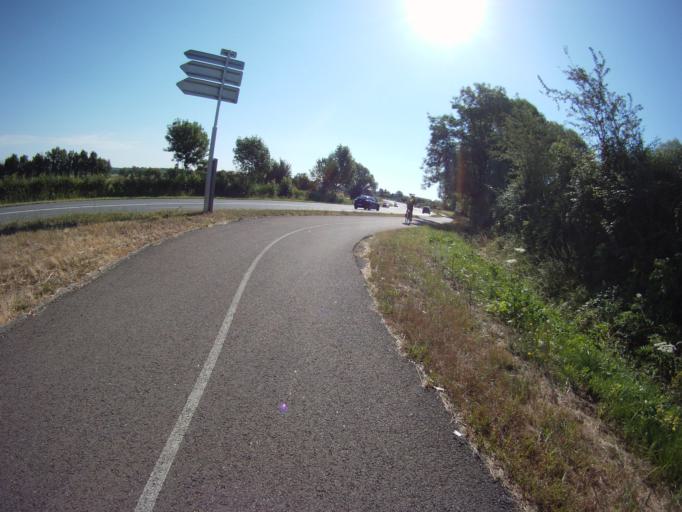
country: FR
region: Bourgogne
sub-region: Departement de la Nievre
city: Marzy
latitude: 46.9954
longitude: 3.1131
